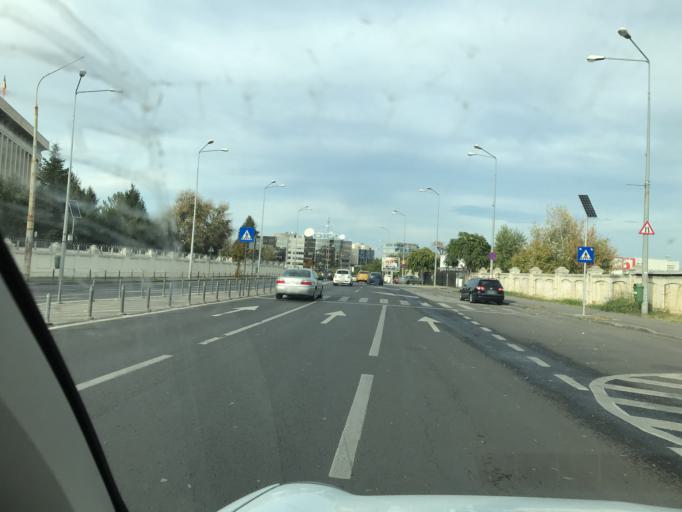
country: RO
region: Bucuresti
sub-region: Municipiul Bucuresti
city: Bucuresti
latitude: 44.4261
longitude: 26.0786
